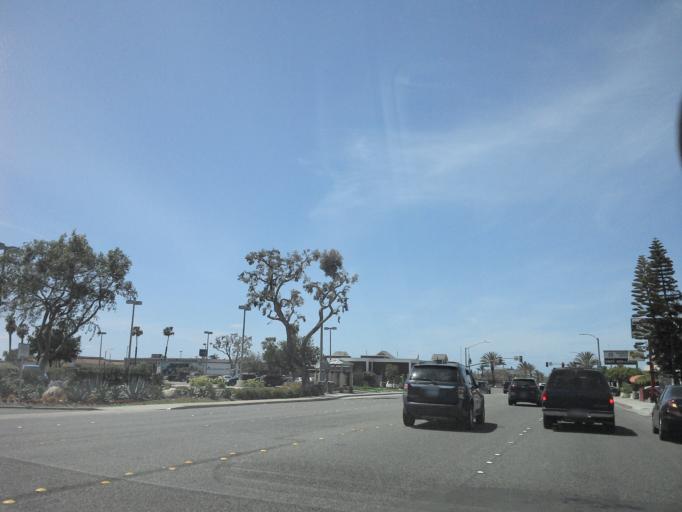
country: US
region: California
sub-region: San Diego County
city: Chula Vista
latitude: 32.6315
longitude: -117.0879
